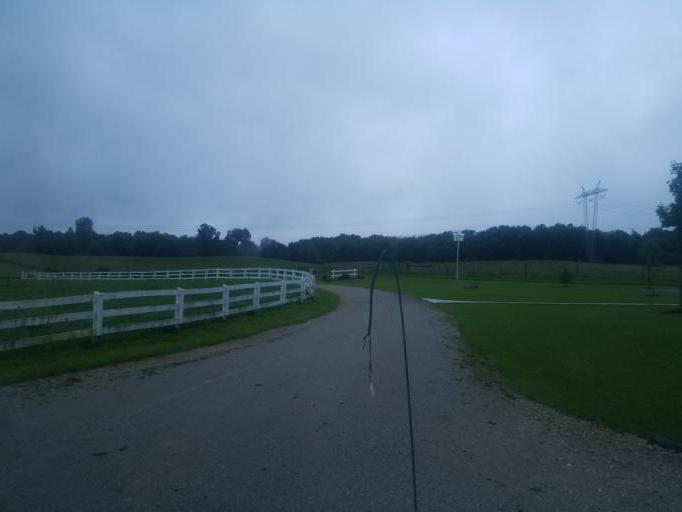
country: US
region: Ohio
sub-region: Richland County
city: Lexington
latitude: 40.5976
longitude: -82.6658
